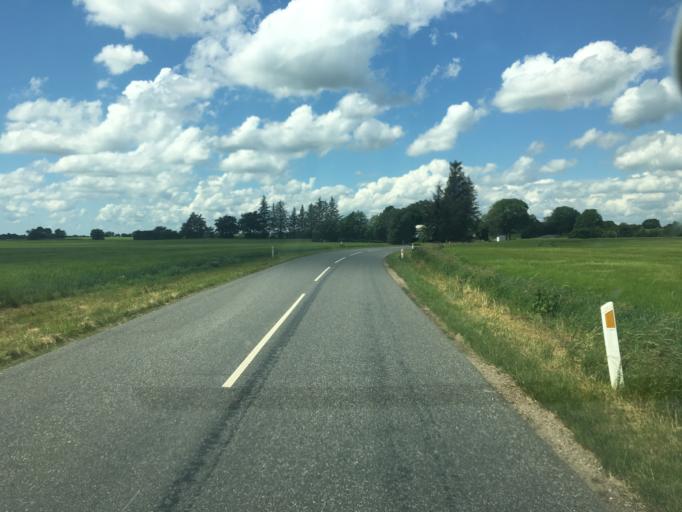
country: DK
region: South Denmark
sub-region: Haderslev Kommune
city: Vojens
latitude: 55.2797
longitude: 9.3204
